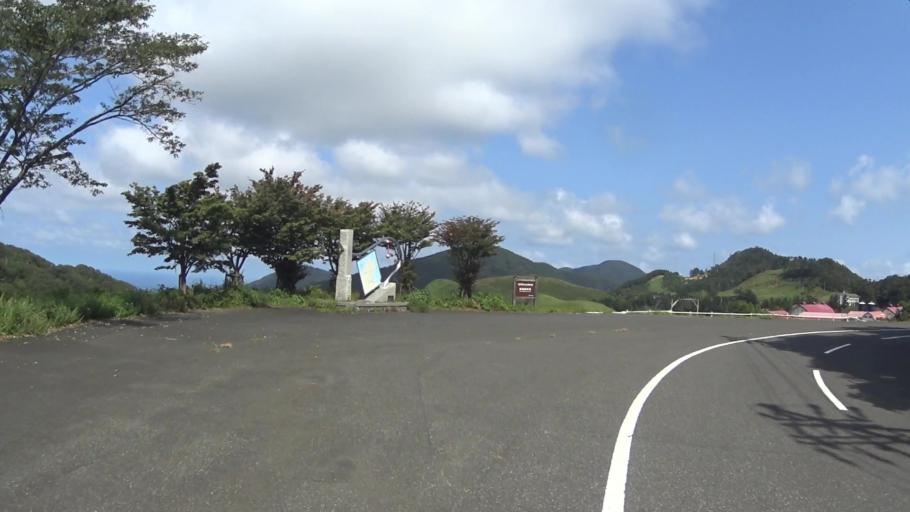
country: JP
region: Kyoto
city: Miyazu
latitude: 35.7188
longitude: 135.1890
